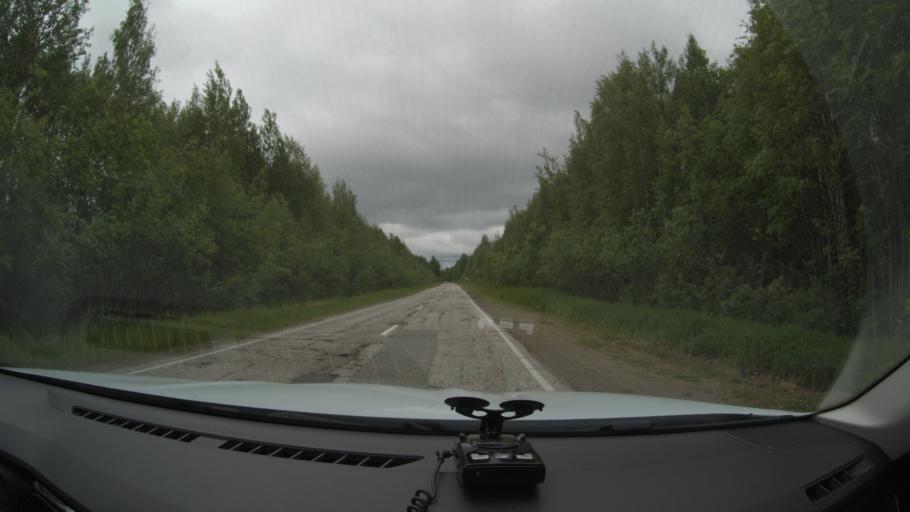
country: RU
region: Komi Republic
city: Nizhniy Odes
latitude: 63.6051
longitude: 54.5130
